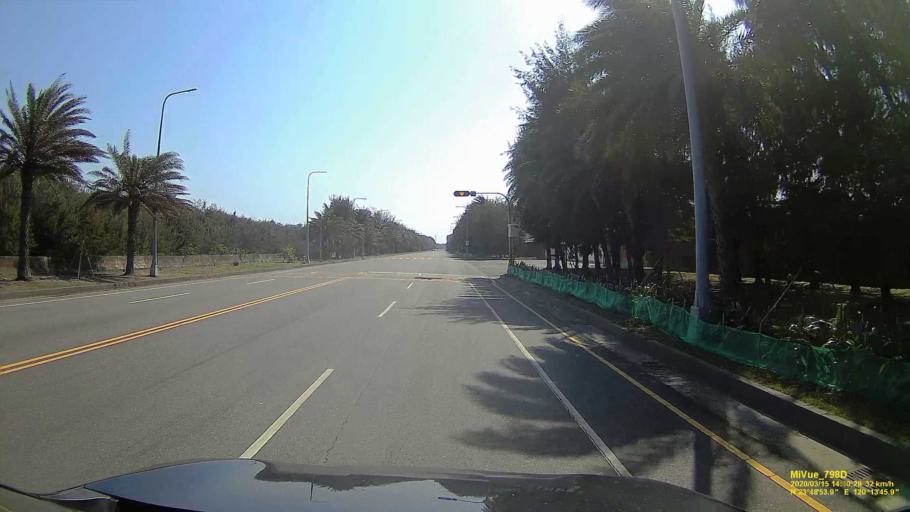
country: TW
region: Taiwan
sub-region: Yunlin
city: Douliu
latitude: 23.8148
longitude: 120.2293
